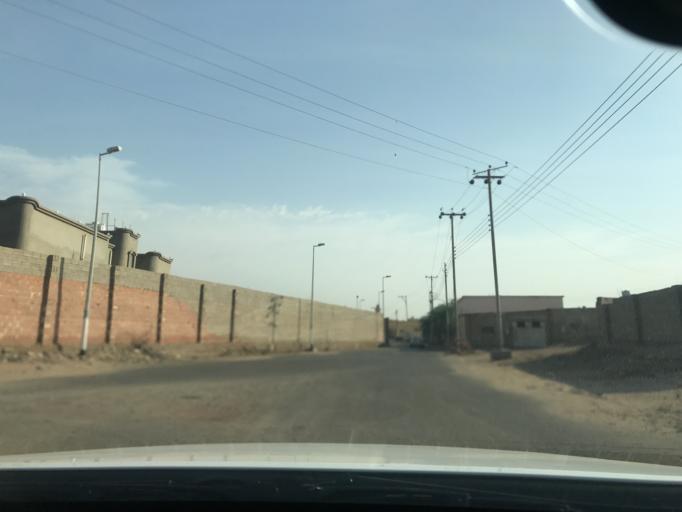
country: SA
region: Makkah
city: Al Jumum
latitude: 21.4496
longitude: 39.5338
